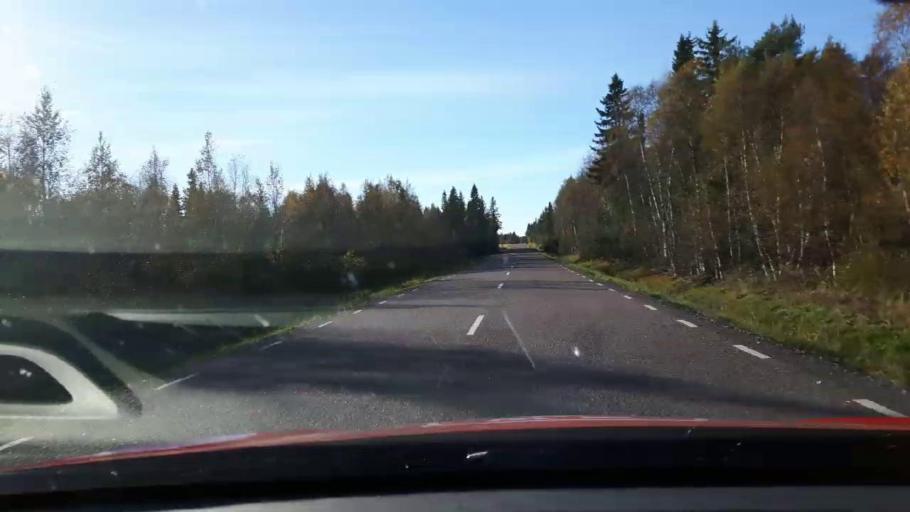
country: SE
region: Jaemtland
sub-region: Stroemsunds Kommun
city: Stroemsund
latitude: 63.8618
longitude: 15.1701
